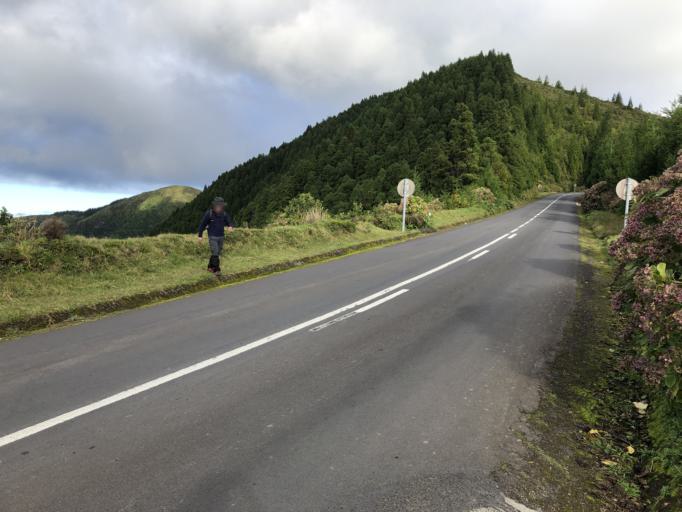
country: PT
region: Azores
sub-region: Ponta Delgada
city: Arrifes
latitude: 37.8379
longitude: -25.7717
